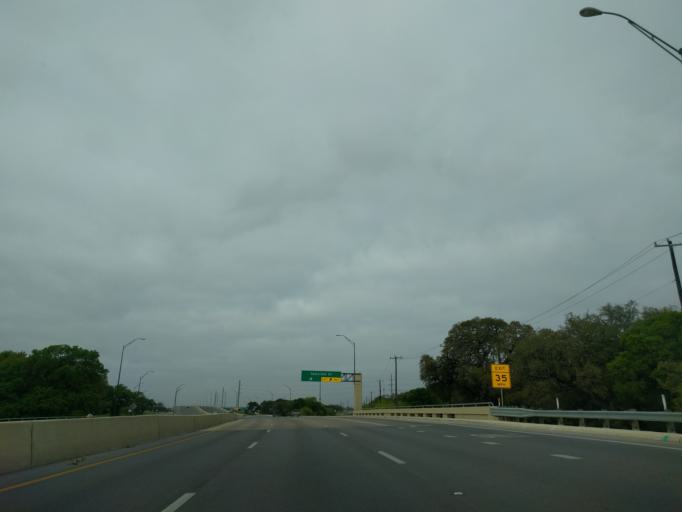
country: US
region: Texas
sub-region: Bexar County
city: Alamo Heights
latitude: 29.5471
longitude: -98.4497
